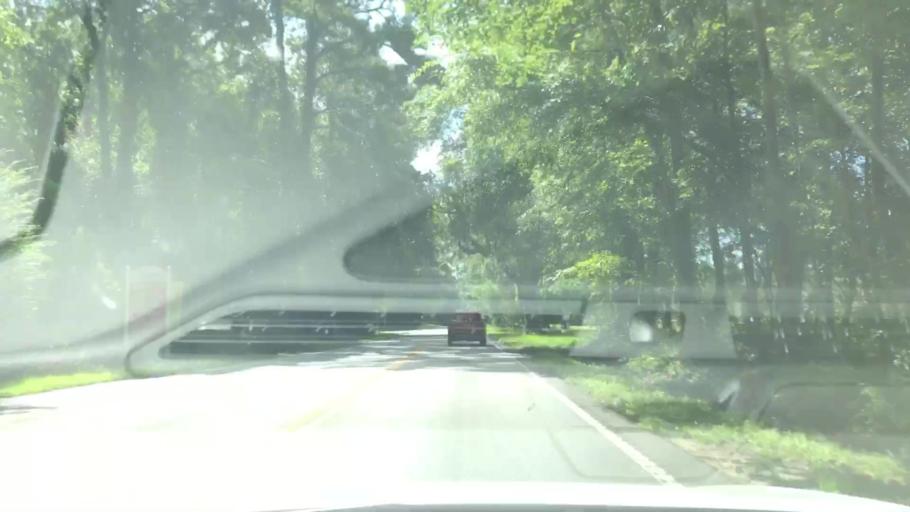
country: US
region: South Carolina
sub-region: Charleston County
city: Shell Point
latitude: 32.8526
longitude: -80.0688
